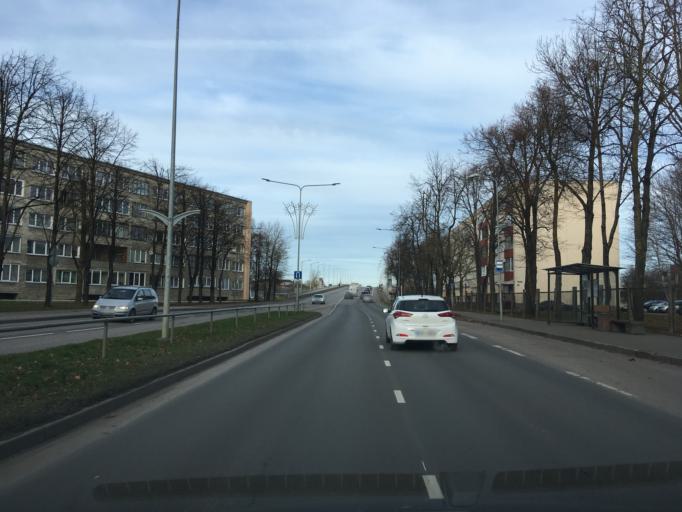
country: EE
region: Ida-Virumaa
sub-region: Narva linn
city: Narva
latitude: 59.3689
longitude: 28.1857
